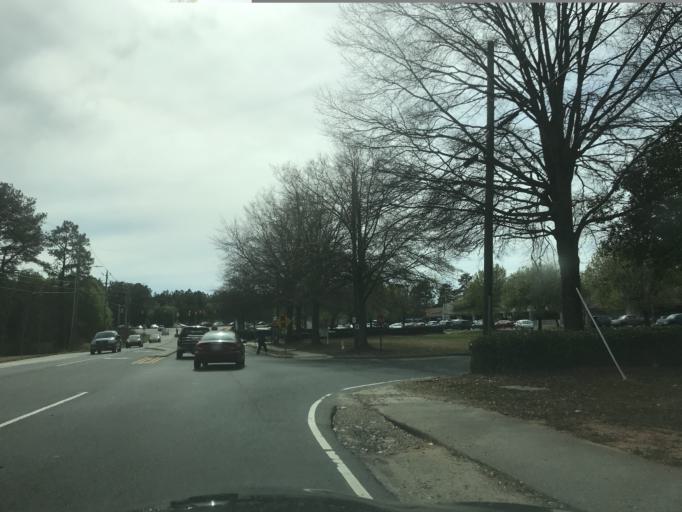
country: US
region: North Carolina
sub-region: Wake County
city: West Raleigh
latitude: 35.7444
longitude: -78.6788
